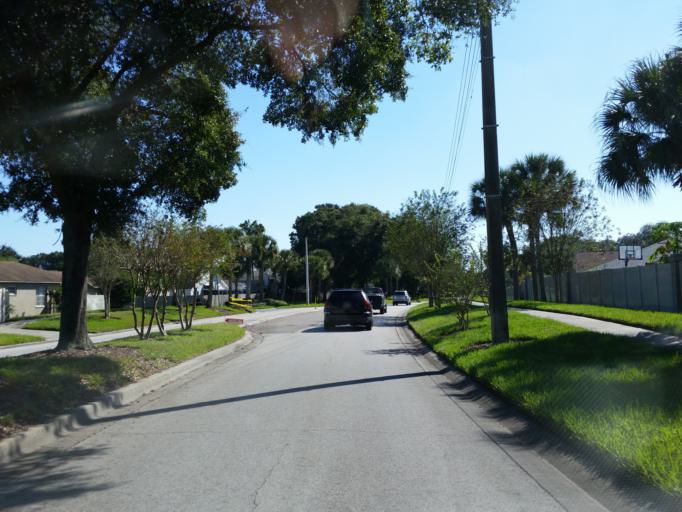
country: US
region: Florida
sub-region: Hillsborough County
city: Brandon
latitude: 27.9255
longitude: -82.2613
